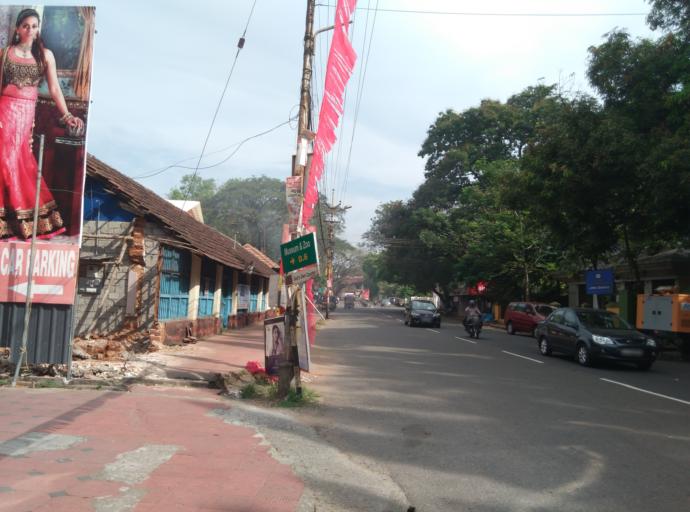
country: IN
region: Kerala
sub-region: Thrissur District
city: Trichur
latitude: 10.5263
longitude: 76.2175
